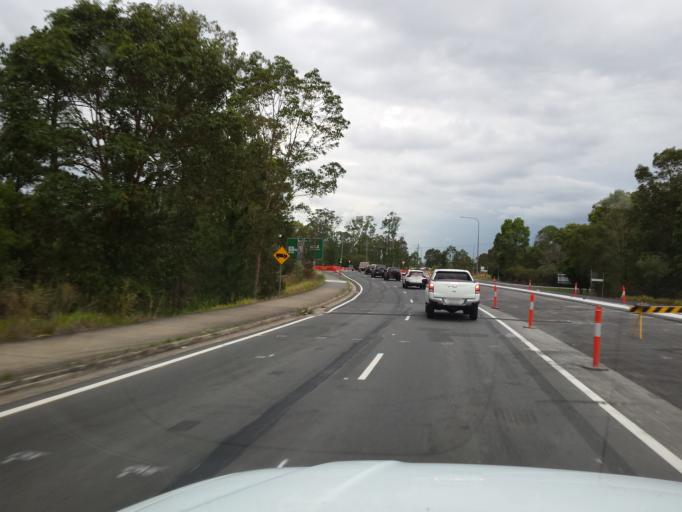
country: AU
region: Queensland
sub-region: Gold Coast
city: Oxenford
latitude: -27.8596
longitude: 153.3114
